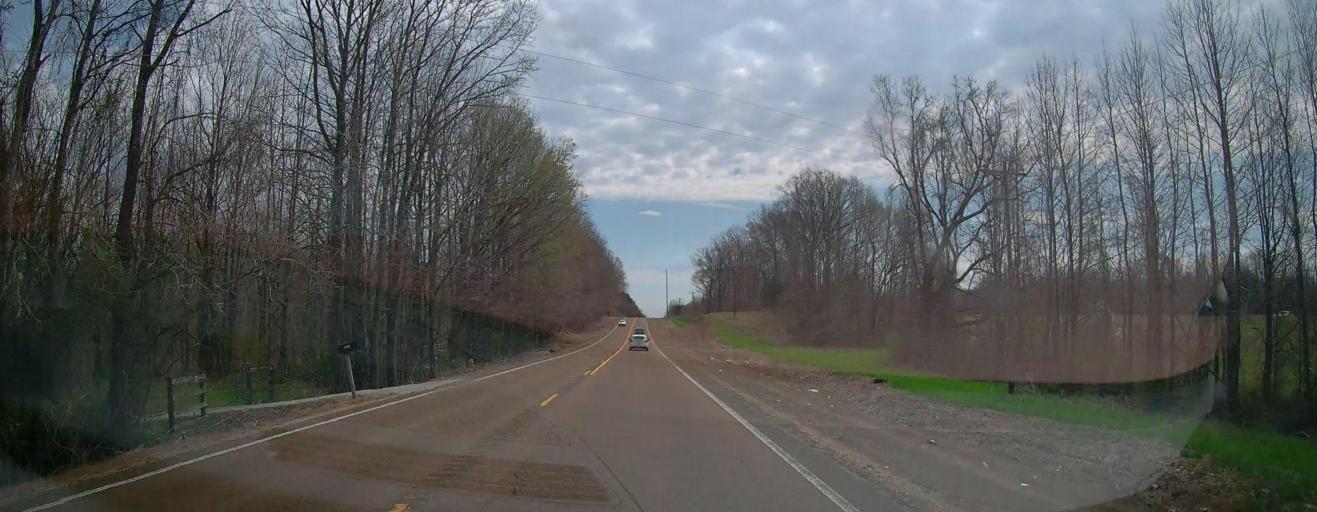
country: US
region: Mississippi
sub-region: Marshall County
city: Holly Springs
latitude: 34.8067
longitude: -89.5089
